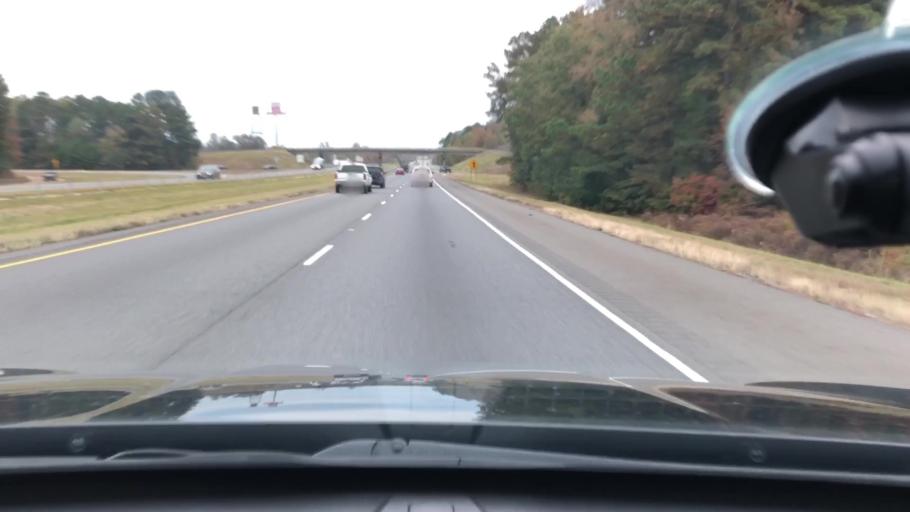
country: US
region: Arkansas
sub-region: Clark County
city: Gurdon
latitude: 33.9949
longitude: -93.1857
